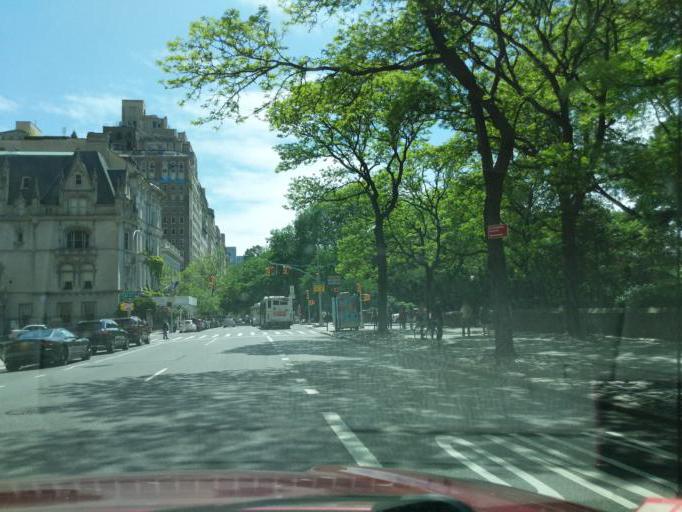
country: US
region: New York
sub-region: New York County
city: Manhattan
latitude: 40.7775
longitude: -73.9633
